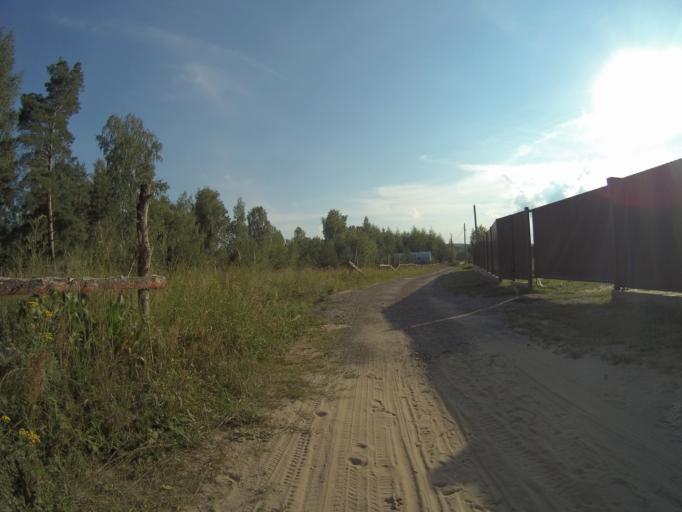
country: RU
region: Vladimir
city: Raduzhnyy
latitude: 56.0280
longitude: 40.3227
